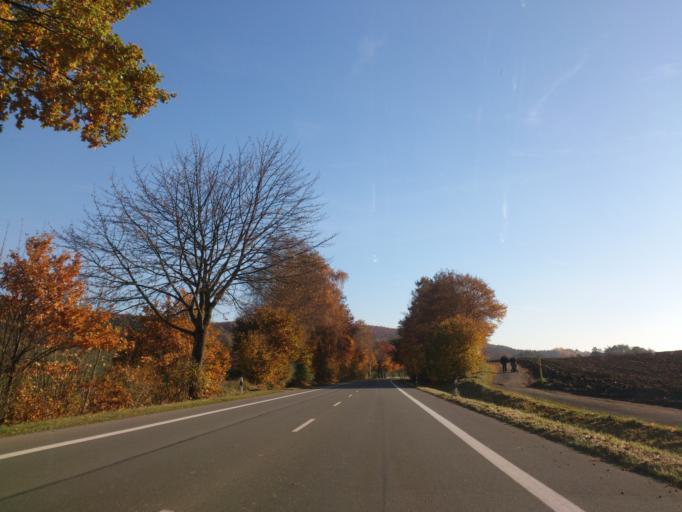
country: DE
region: North Rhine-Westphalia
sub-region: Regierungsbezirk Detmold
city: Willebadessen
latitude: 51.6170
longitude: 9.0327
